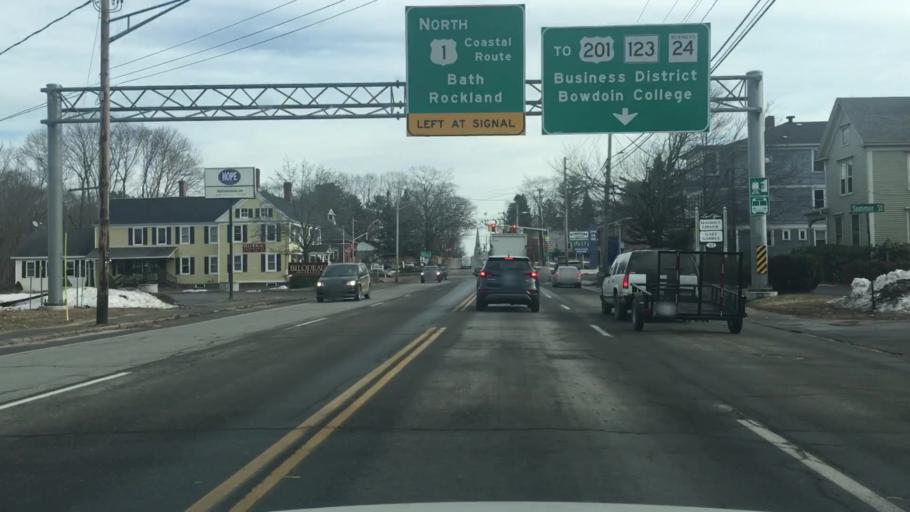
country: US
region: Maine
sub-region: Cumberland County
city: Brunswick
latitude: 43.9129
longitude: -69.9779
